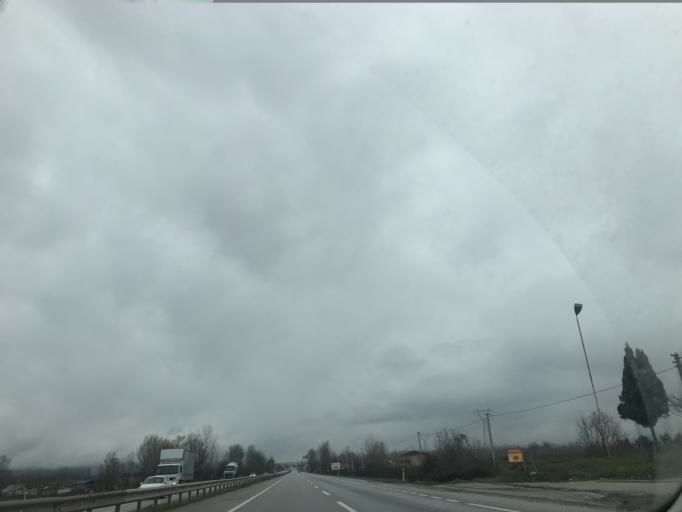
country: TR
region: Sakarya
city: Akyazi
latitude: 40.7718
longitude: 30.6348
